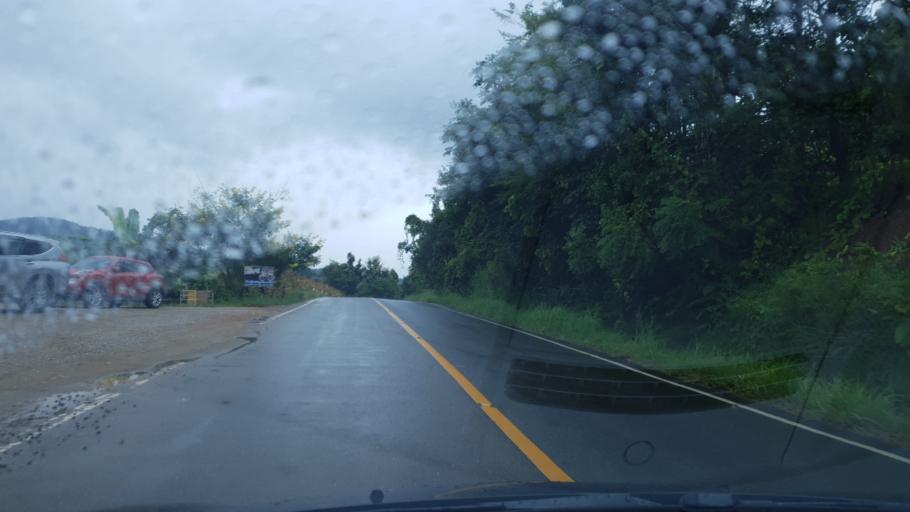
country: TH
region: Mae Hong Son
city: Mae La Noi
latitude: 18.5402
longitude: 97.9382
